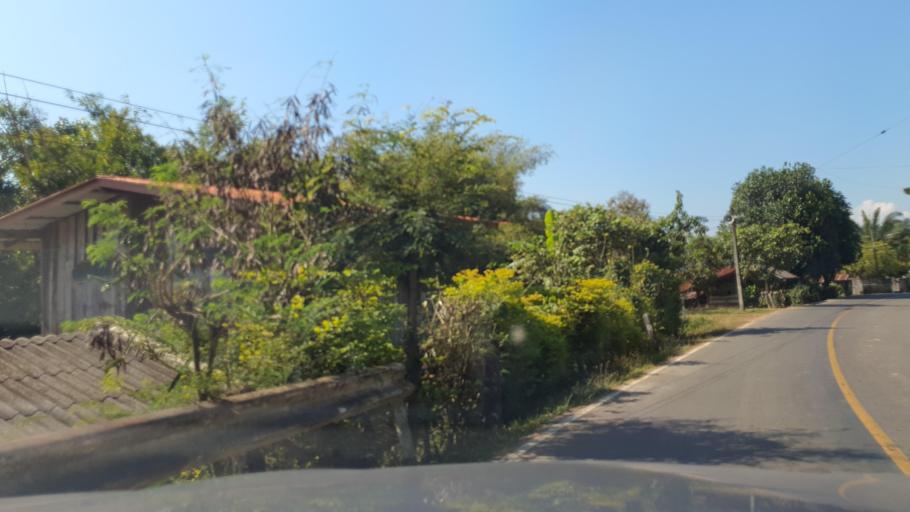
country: TH
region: Nan
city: Pua
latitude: 19.1132
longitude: 100.9132
